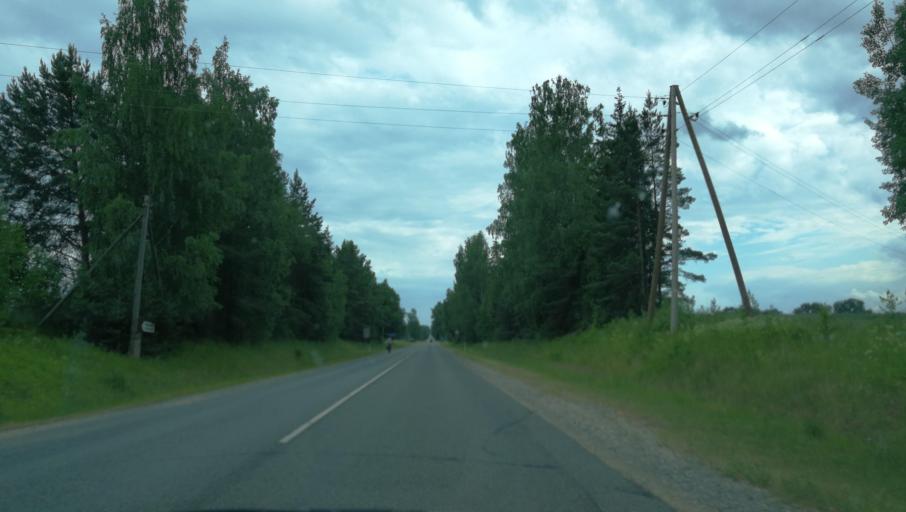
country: LV
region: Naukseni
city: Naukseni
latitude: 57.7222
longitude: 25.4227
